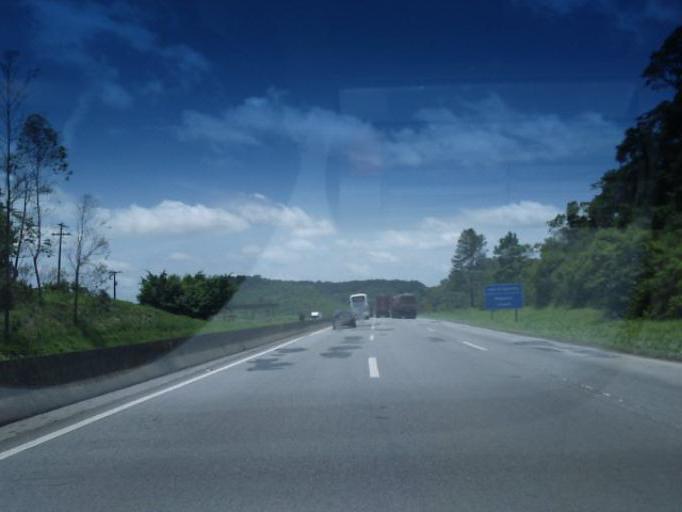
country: BR
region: Sao Paulo
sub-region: Juquia
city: Juquia
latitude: -24.3937
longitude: -47.7249
